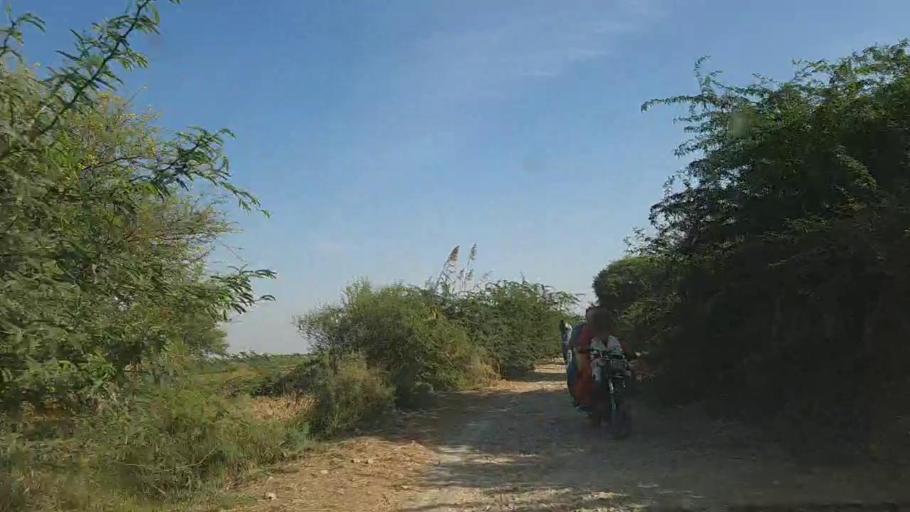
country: PK
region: Sindh
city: Bulri
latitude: 24.8049
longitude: 68.3302
